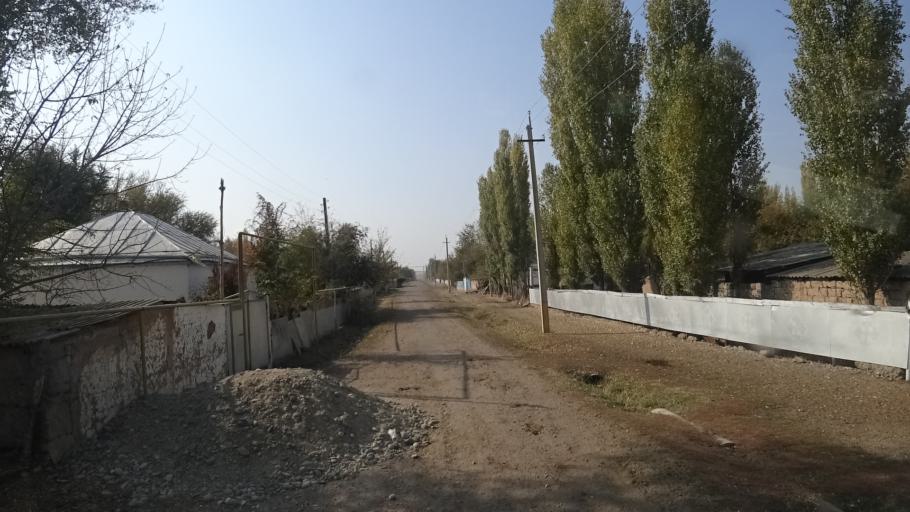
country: KZ
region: Zhambyl
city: Sarykemer
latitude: 43.0756
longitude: 71.6163
